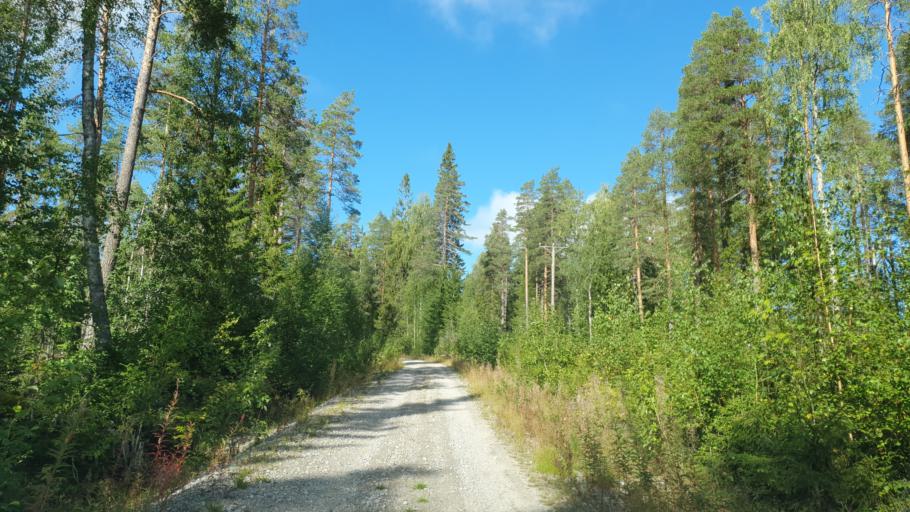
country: FI
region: Kainuu
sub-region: Kehys-Kainuu
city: Kuhmo
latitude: 64.0398
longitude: 29.1370
